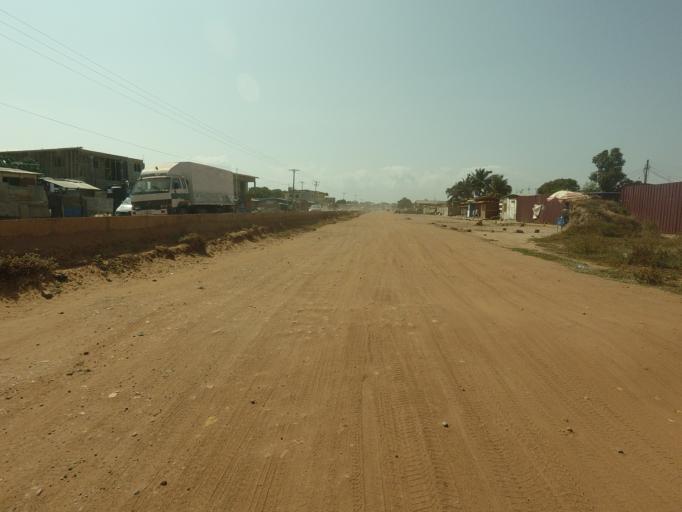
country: GH
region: Greater Accra
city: Teshi Old Town
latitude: 5.5828
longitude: -0.1133
